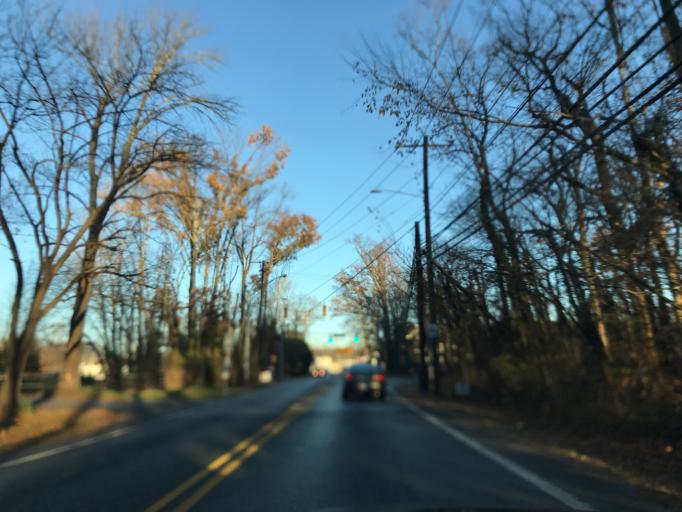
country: US
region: Maryland
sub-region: Montgomery County
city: Ashton-Sandy Spring
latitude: 39.1488
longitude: -77.0302
